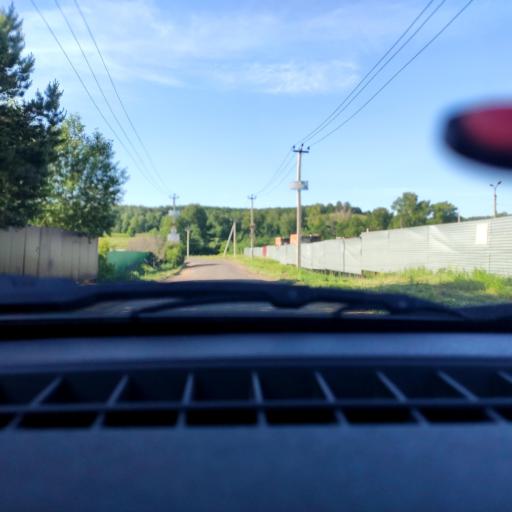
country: RU
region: Bashkortostan
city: Avdon
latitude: 54.4605
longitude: 55.8481
